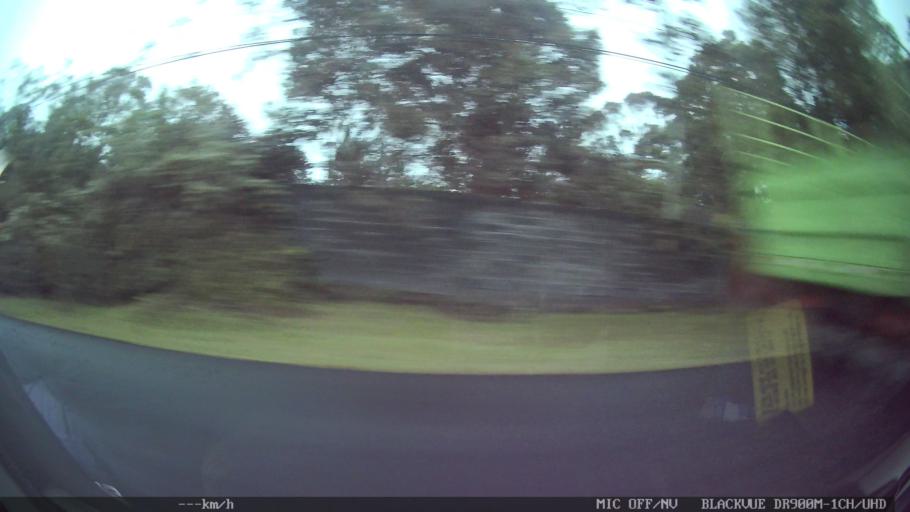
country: ID
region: Bali
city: Klau
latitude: -8.3539
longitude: 115.0312
